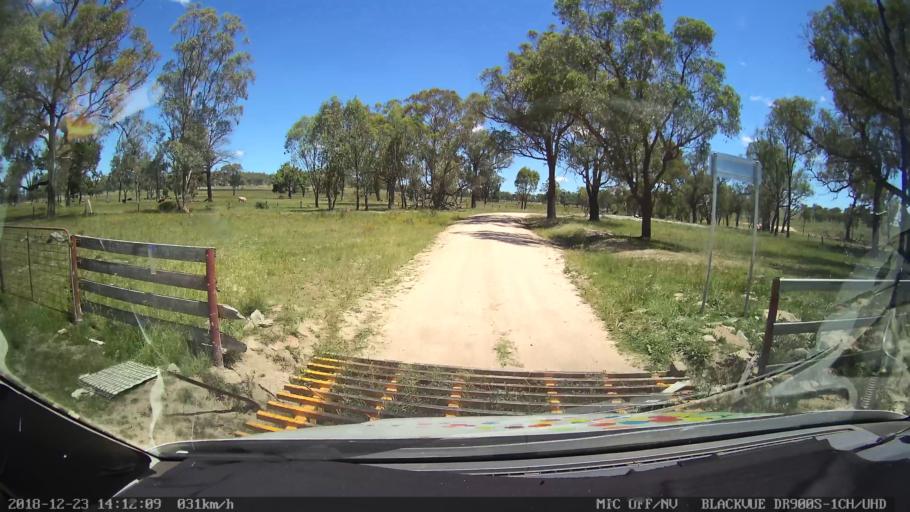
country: AU
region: New South Wales
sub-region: Tamworth Municipality
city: Manilla
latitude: -30.6540
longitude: 151.0466
